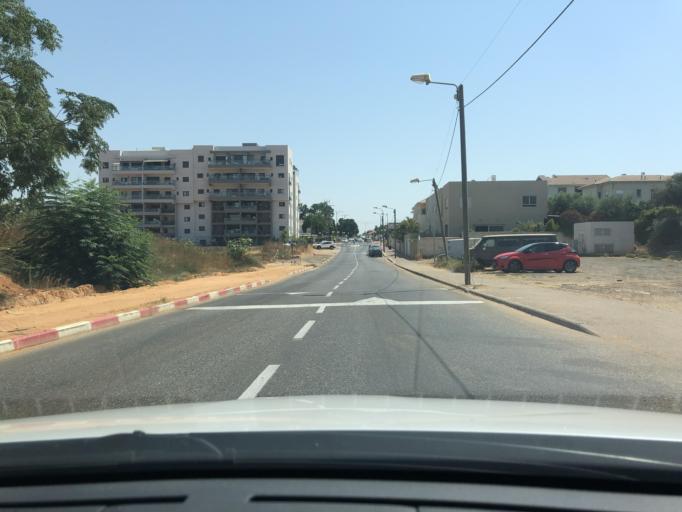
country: IL
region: Central District
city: Kfar Saba
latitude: 32.1622
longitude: 34.9115
